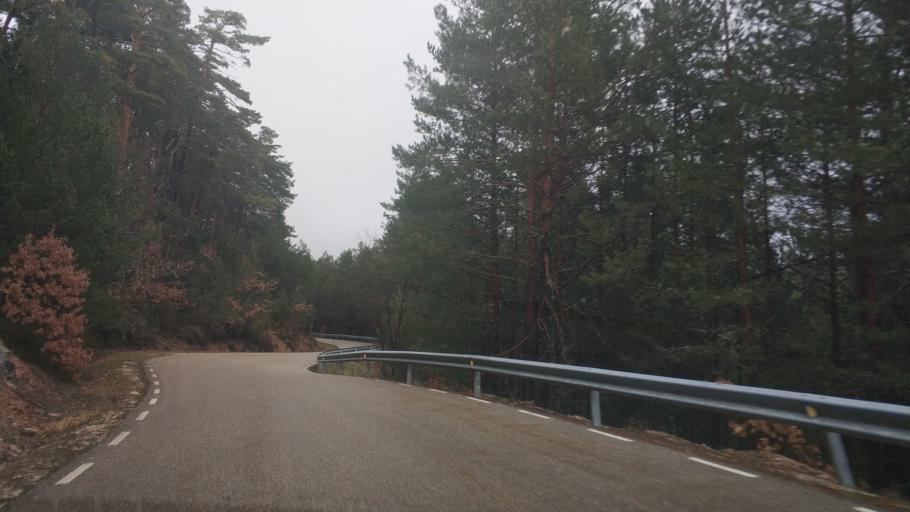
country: ES
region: Castille and Leon
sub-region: Provincia de Burgos
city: Quintanar de la Sierra
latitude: 42.0108
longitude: -3.0198
